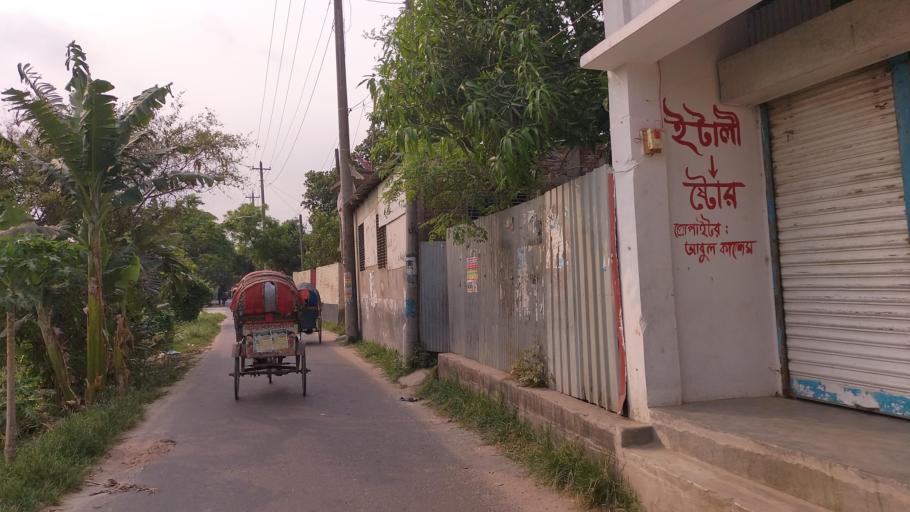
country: BD
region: Dhaka
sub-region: Dhaka
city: Dhaka
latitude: 23.6656
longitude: 90.3511
